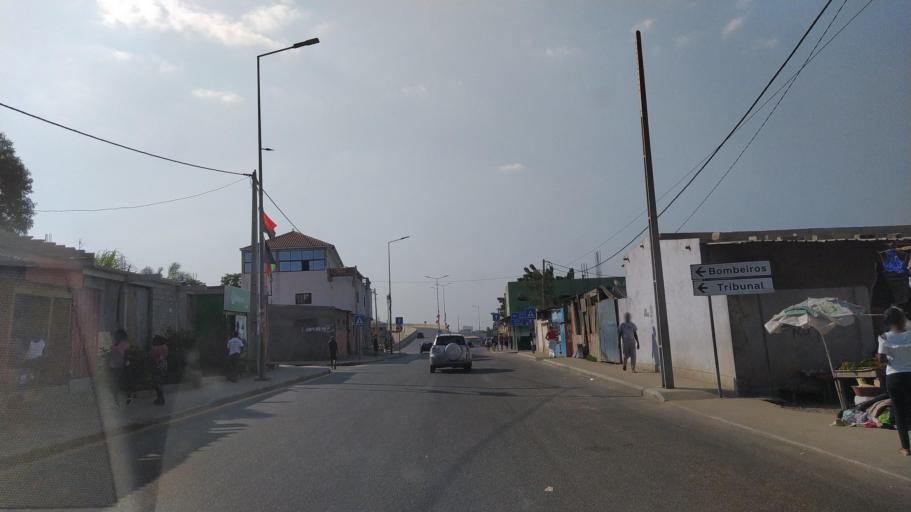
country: AO
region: Luanda
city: Luanda
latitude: -8.8820
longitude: 13.2580
